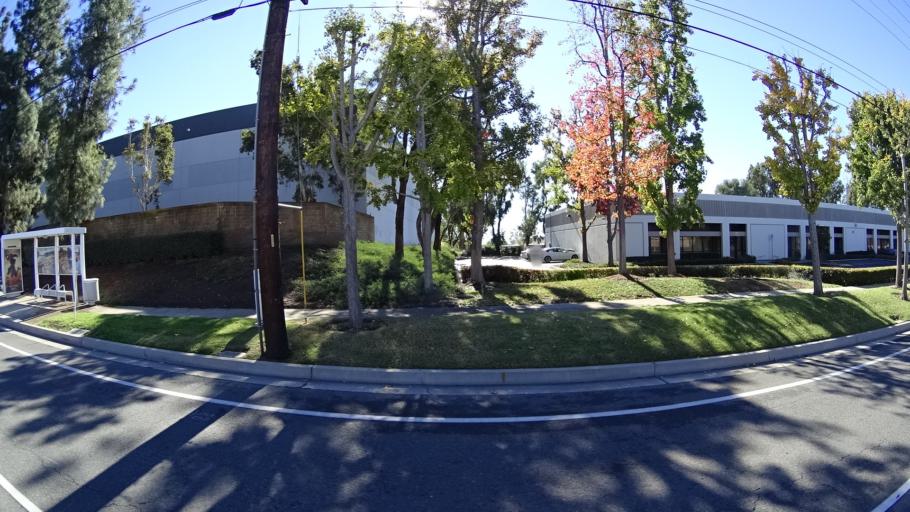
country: US
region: California
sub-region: Orange County
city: Brea
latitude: 33.9318
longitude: -117.9121
